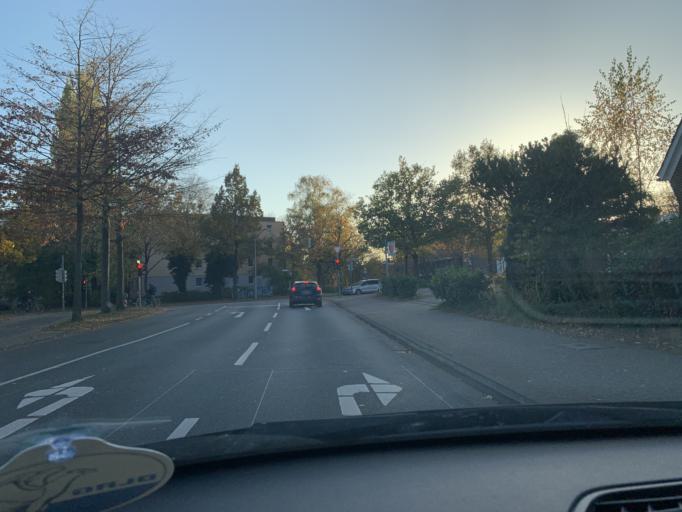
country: DE
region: Lower Saxony
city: Oldenburg
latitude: 53.1415
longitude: 8.1758
